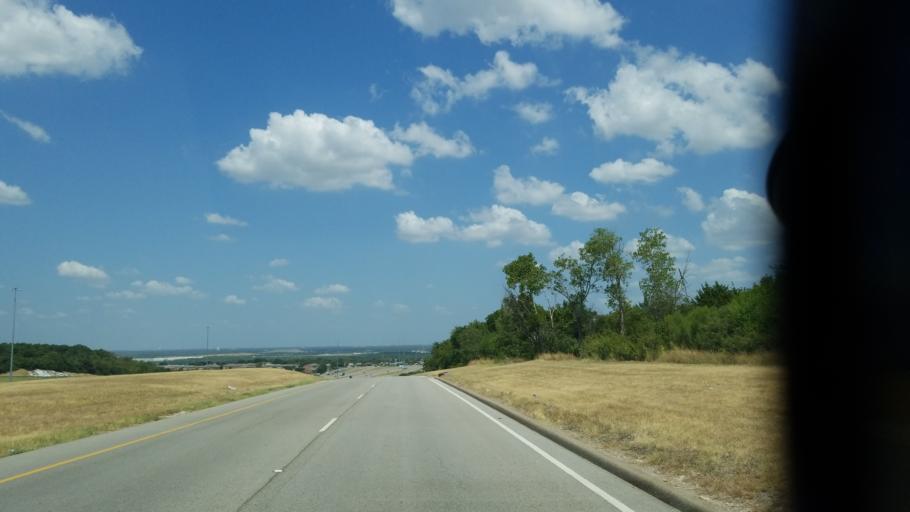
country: US
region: Texas
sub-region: Dallas County
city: Cockrell Hill
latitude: 32.7239
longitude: -96.9164
